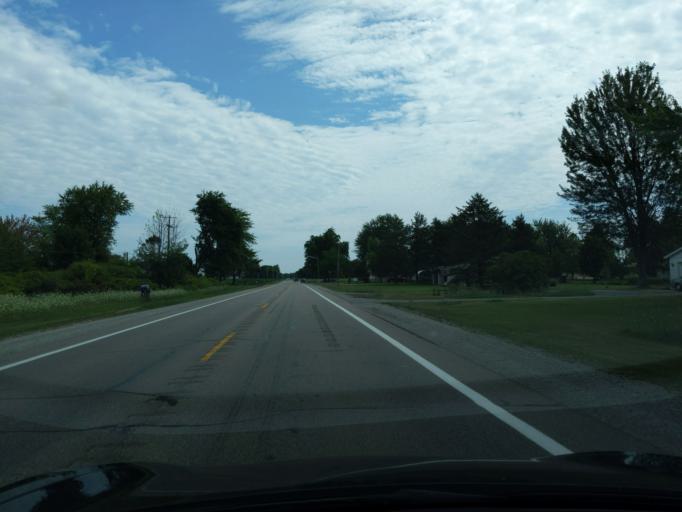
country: US
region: Michigan
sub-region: Gratiot County
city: Breckenridge
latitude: 43.4080
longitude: -84.3914
